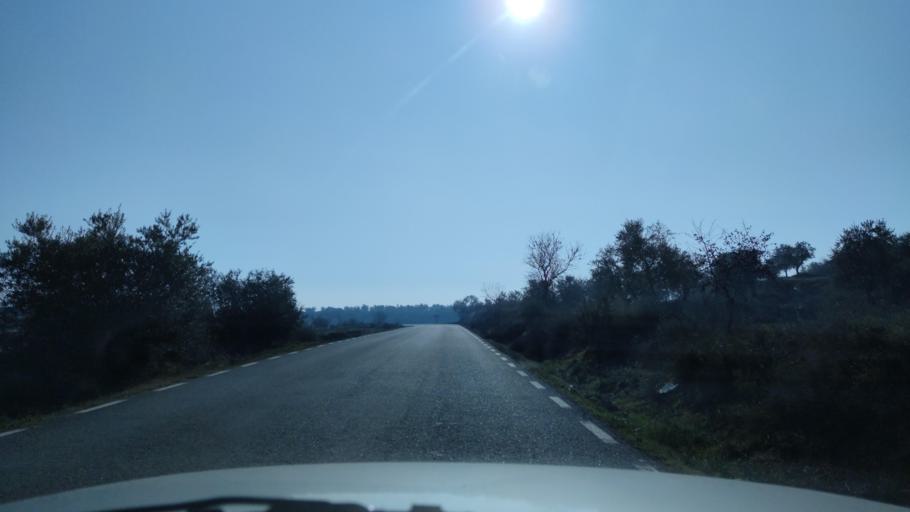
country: ES
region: Catalonia
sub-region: Provincia de Lleida
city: Torrebesses
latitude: 41.4699
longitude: 0.5620
